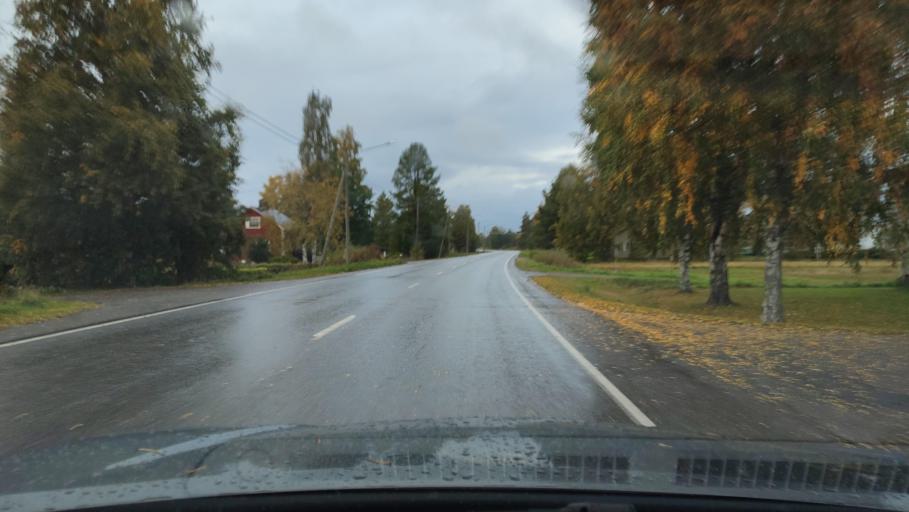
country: FI
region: Southern Ostrobothnia
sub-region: Suupohja
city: Karijoki
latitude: 62.2315
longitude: 21.6243
